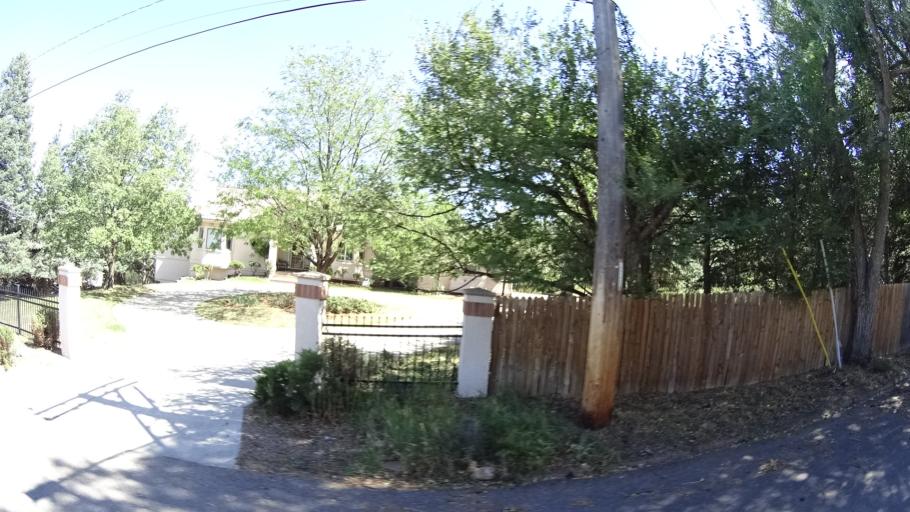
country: US
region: Colorado
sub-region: El Paso County
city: Colorado Springs
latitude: 38.7855
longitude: -104.8600
